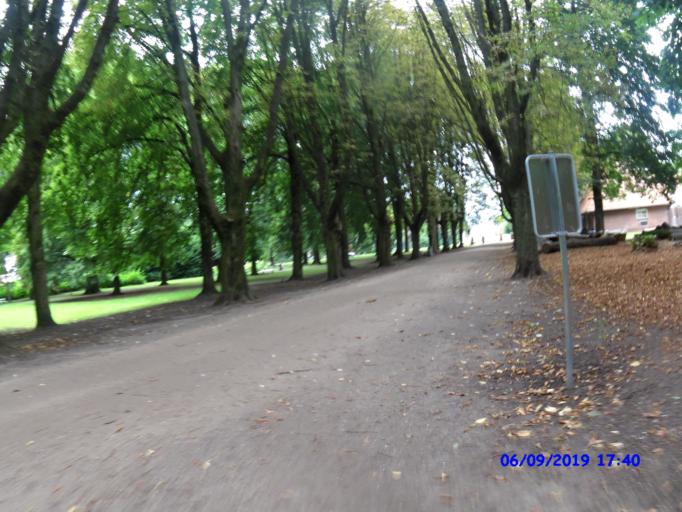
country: BE
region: Flanders
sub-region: Provincie Antwerpen
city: Turnhout
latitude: 51.3114
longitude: 4.9444
